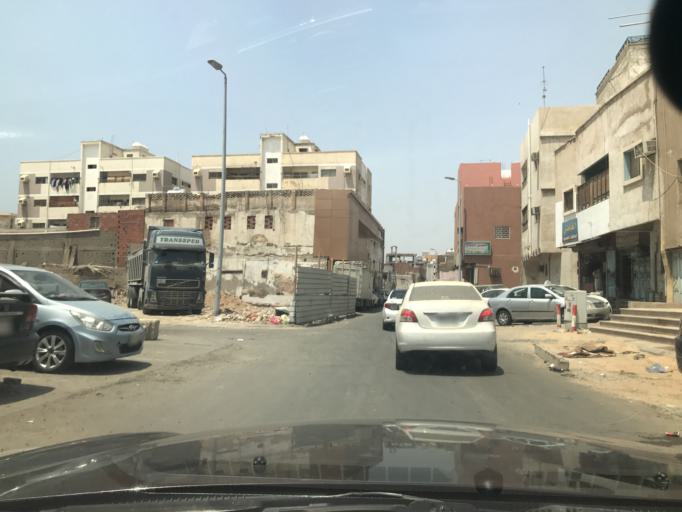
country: SA
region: Makkah
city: Jeddah
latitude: 21.4722
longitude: 39.1857
